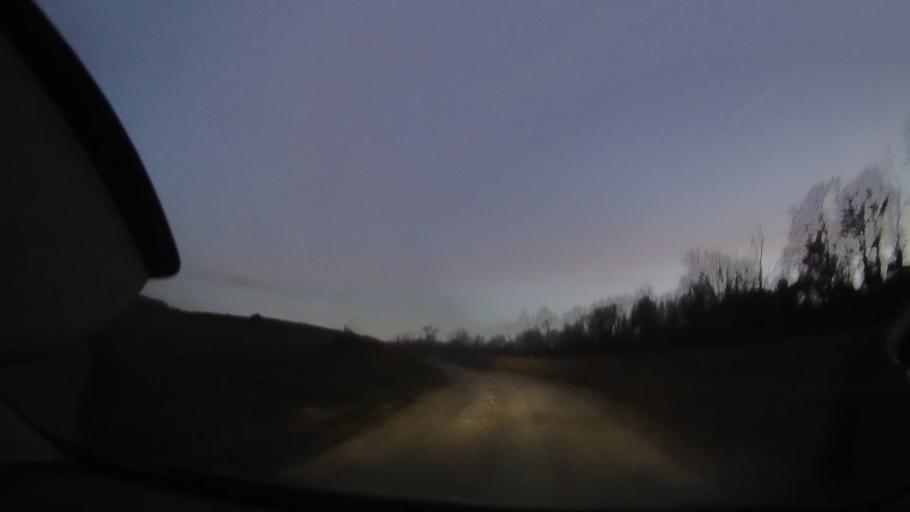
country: RO
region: Bihor
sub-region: Comuna Tetchea
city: Hotar
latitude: 47.0043
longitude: 22.3085
